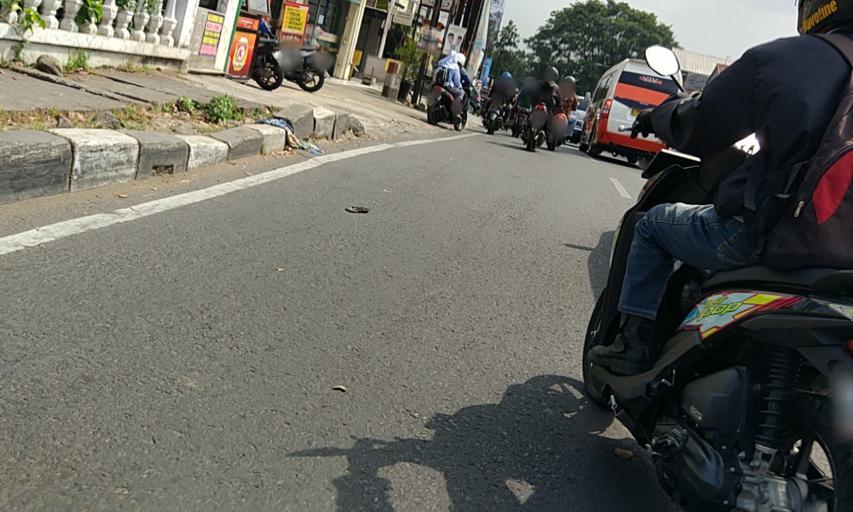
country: ID
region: West Java
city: Bandung
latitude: -6.9048
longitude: 107.6779
